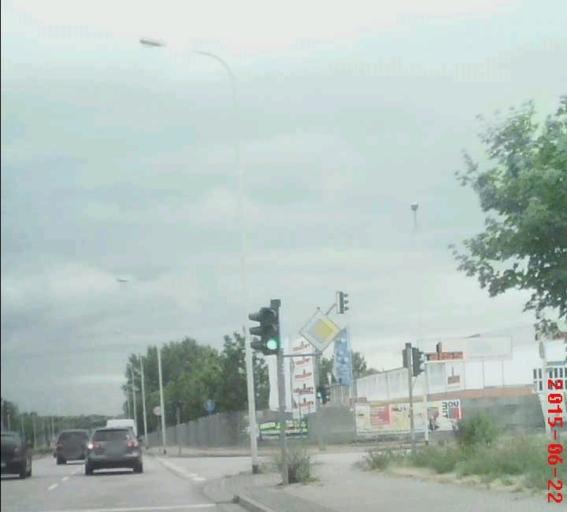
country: DE
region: Saxony-Anhalt
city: Angersdorf
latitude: 51.4702
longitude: 11.8971
